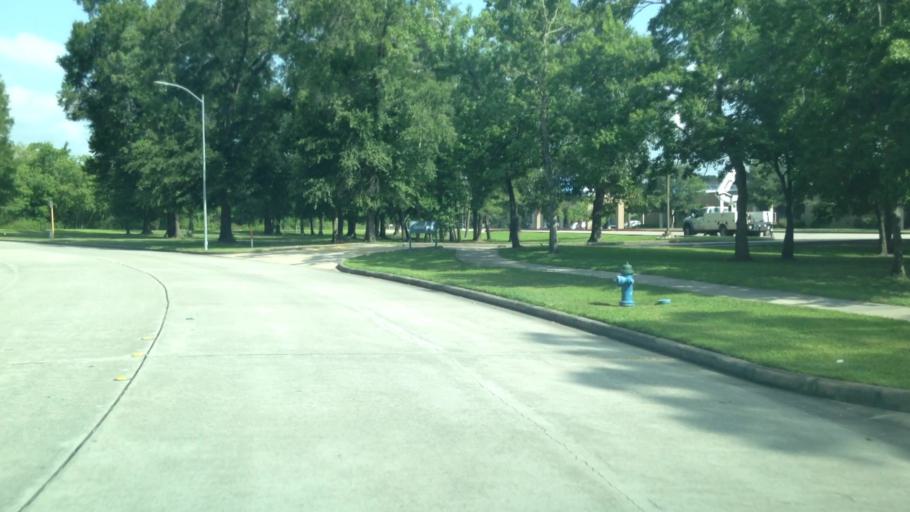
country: US
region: Texas
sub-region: Harris County
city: Atascocita
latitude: 29.9263
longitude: -95.1762
